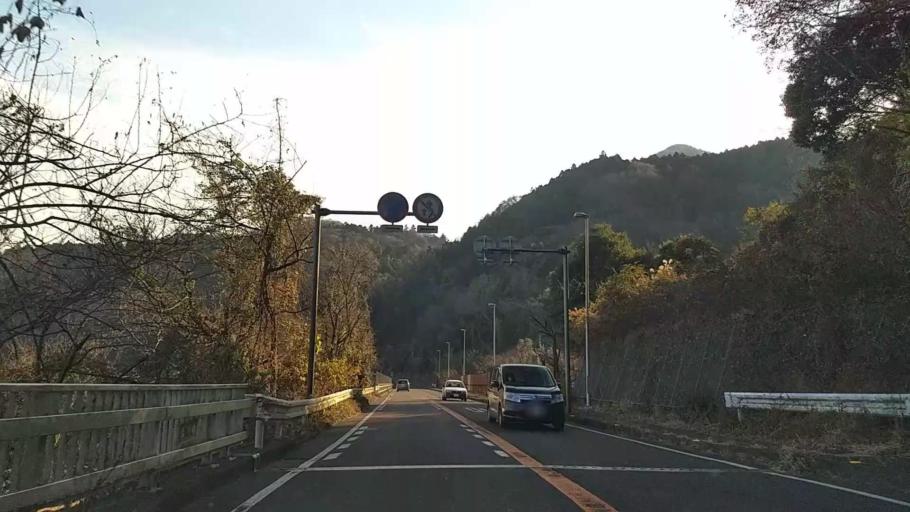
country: JP
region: Kanagawa
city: Zama
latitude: 35.5278
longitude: 139.2806
